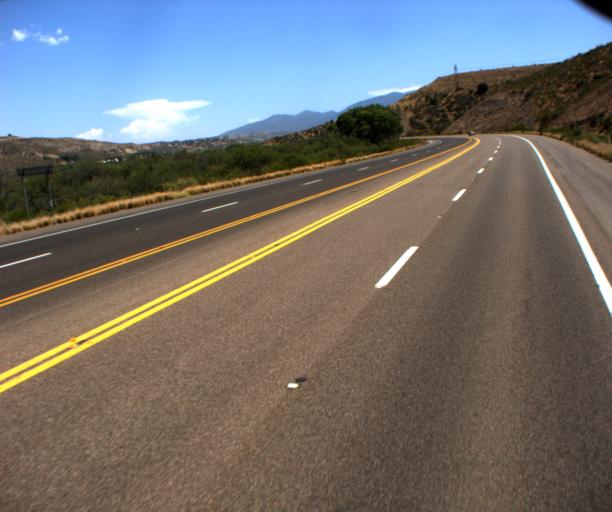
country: US
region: Arizona
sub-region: Gila County
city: Claypool
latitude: 33.4474
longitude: -110.8382
